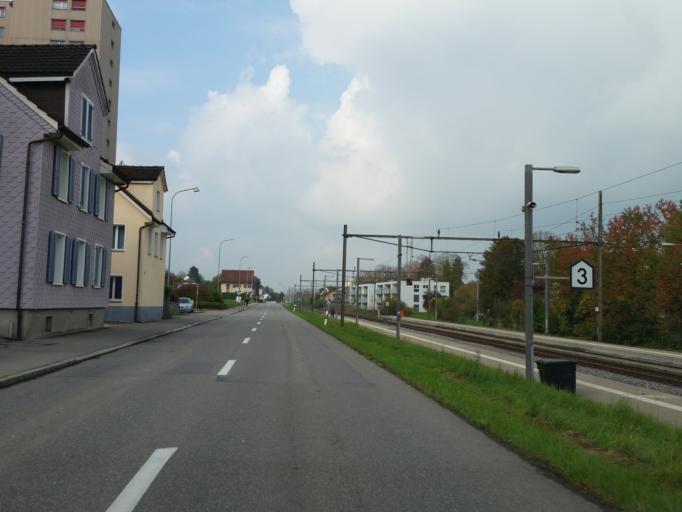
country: CH
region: Thurgau
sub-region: Arbon District
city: Amriswil
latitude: 47.5507
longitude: 9.2994
